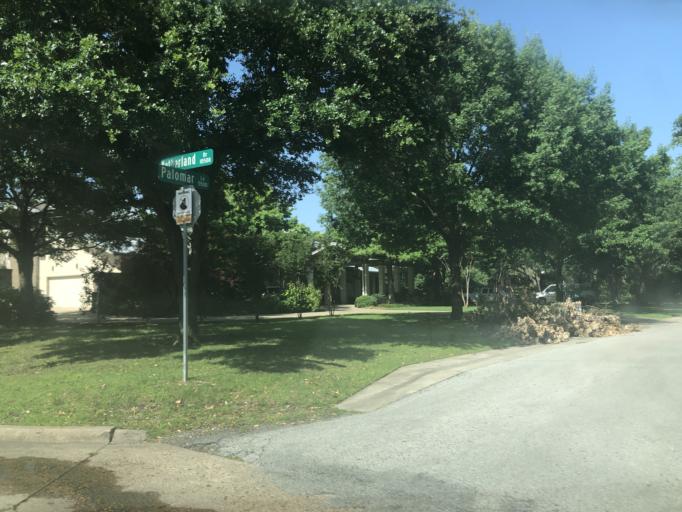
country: US
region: Texas
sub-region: Dallas County
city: University Park
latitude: 32.8896
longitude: -96.8125
